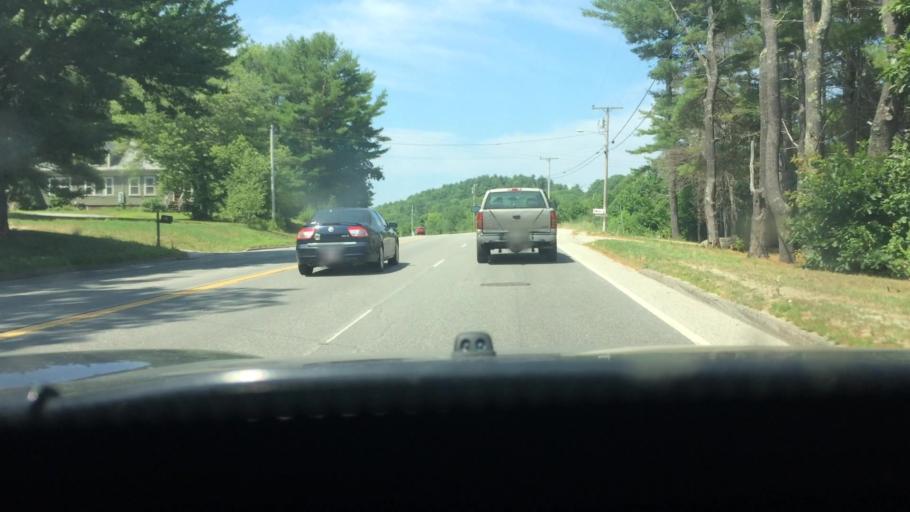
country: US
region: Maine
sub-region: Androscoggin County
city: Minot
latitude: 44.0806
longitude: -70.2823
